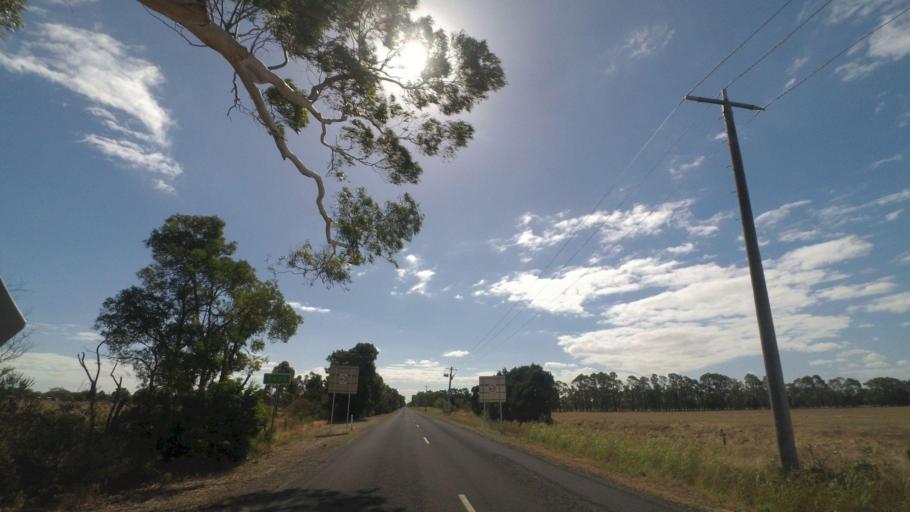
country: AU
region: Victoria
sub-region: Cardinia
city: Pakenham South
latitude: -38.1754
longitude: 145.5652
